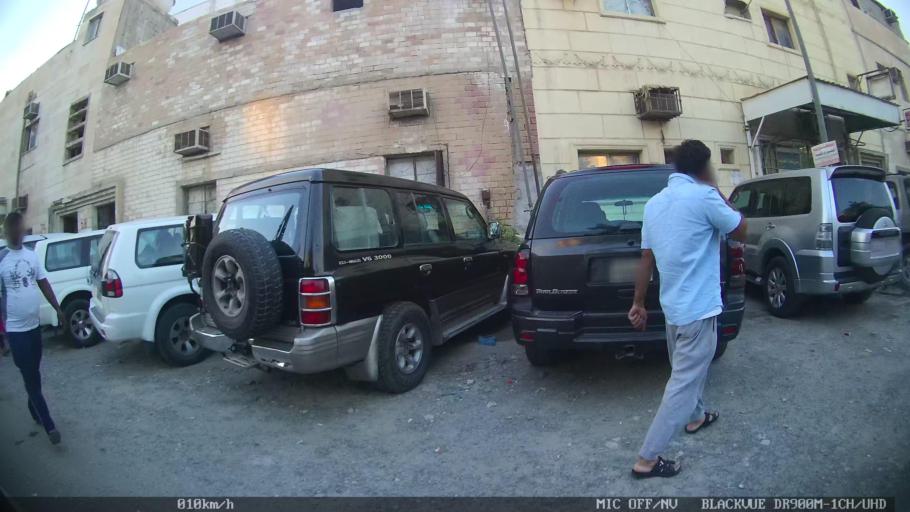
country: KW
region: Al Farwaniyah
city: Janub as Surrah
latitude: 29.2867
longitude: 47.9790
